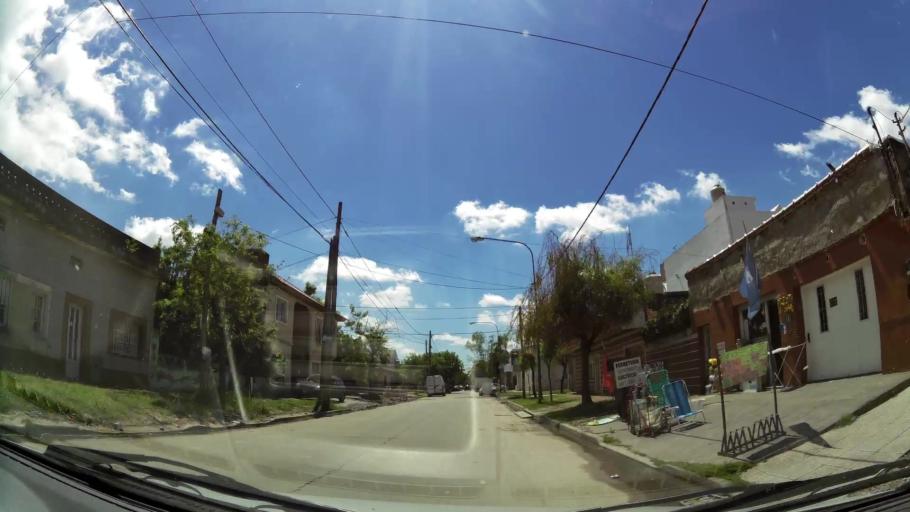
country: AR
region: Buenos Aires
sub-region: Partido de Lanus
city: Lanus
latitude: -34.7021
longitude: -58.4224
